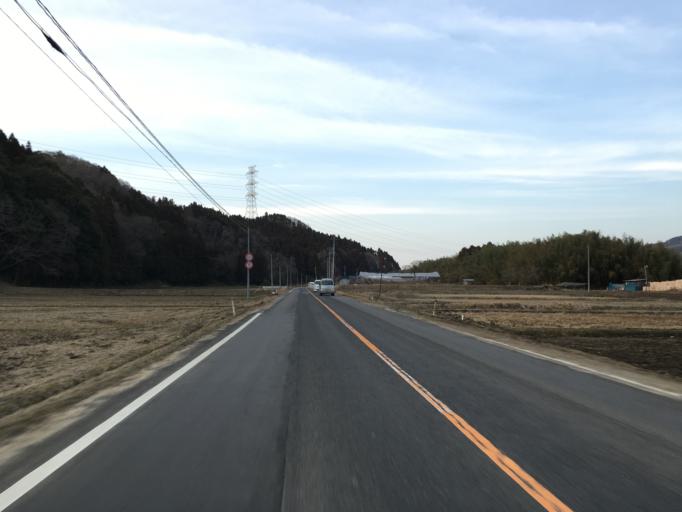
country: JP
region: Ibaraki
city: Daigo
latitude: 36.8867
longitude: 140.4119
